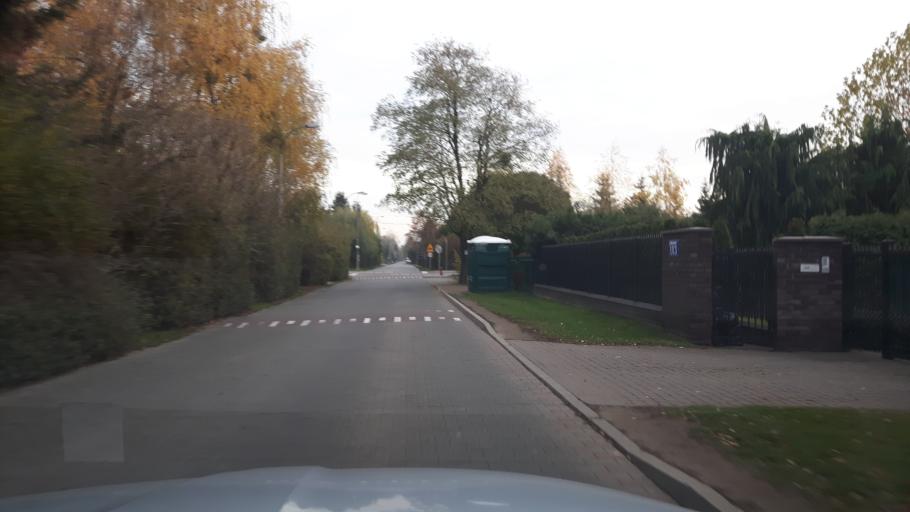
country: PL
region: Masovian Voivodeship
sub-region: Warszawa
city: Wilanow
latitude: 52.1694
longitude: 21.1154
